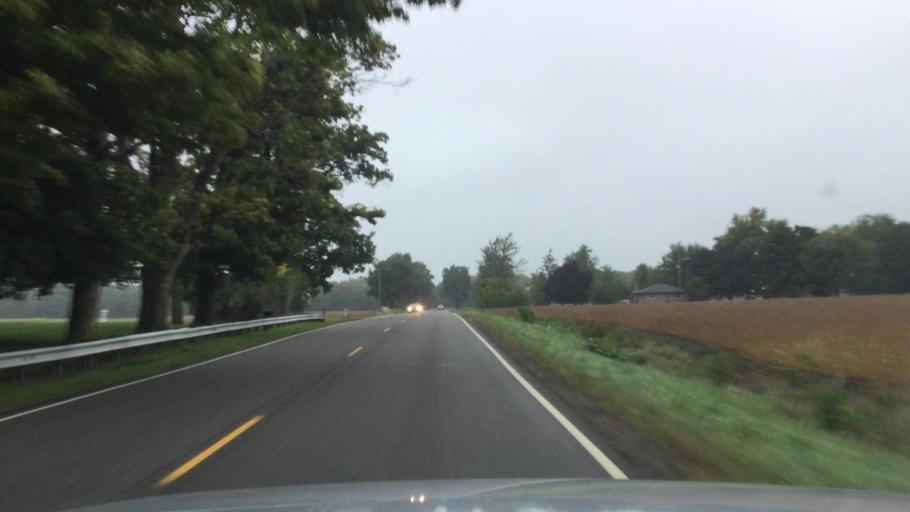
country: US
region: Michigan
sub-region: Shiawassee County
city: Corunna
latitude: 42.9261
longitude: -84.1242
